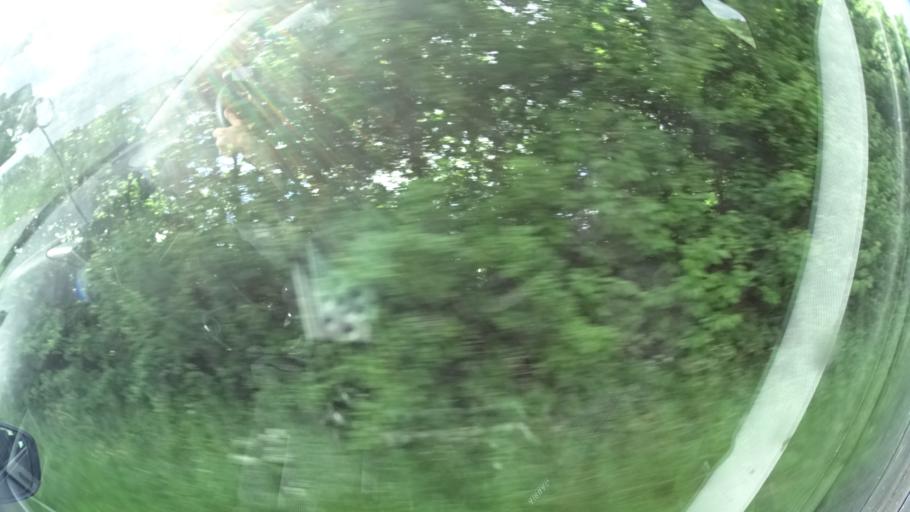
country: DK
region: Central Jutland
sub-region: Syddjurs Kommune
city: Ronde
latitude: 56.3122
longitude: 10.4171
